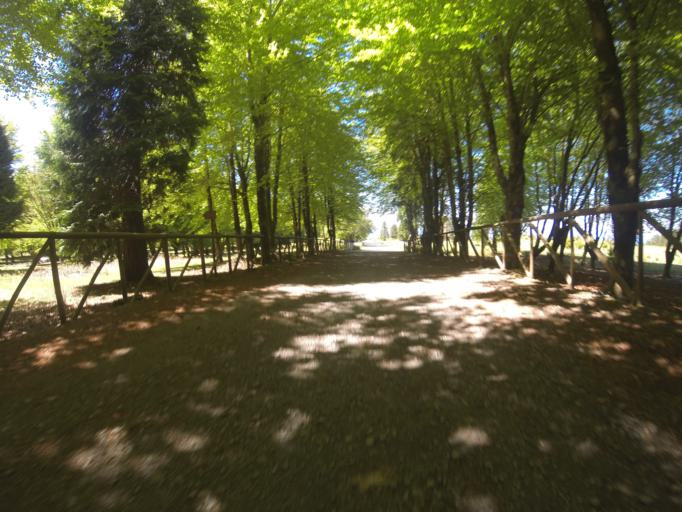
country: PT
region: Madeira
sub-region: Funchal
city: Nossa Senhora do Monte
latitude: 32.7237
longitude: -16.8865
